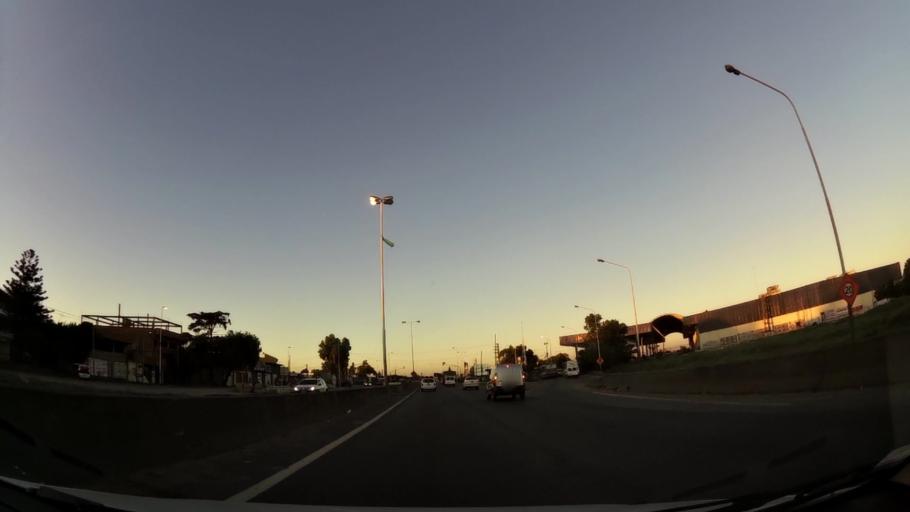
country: AR
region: Buenos Aires
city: Pontevedra
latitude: -34.7557
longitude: -58.6149
